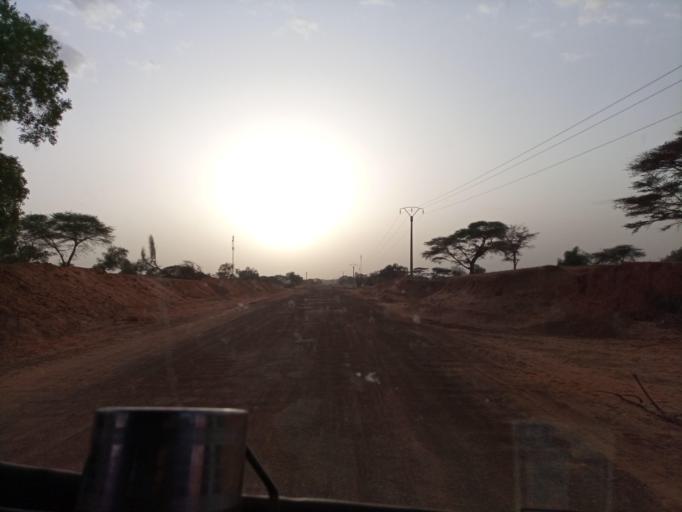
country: SN
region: Louga
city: Dara
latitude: 15.3970
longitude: -15.6482
